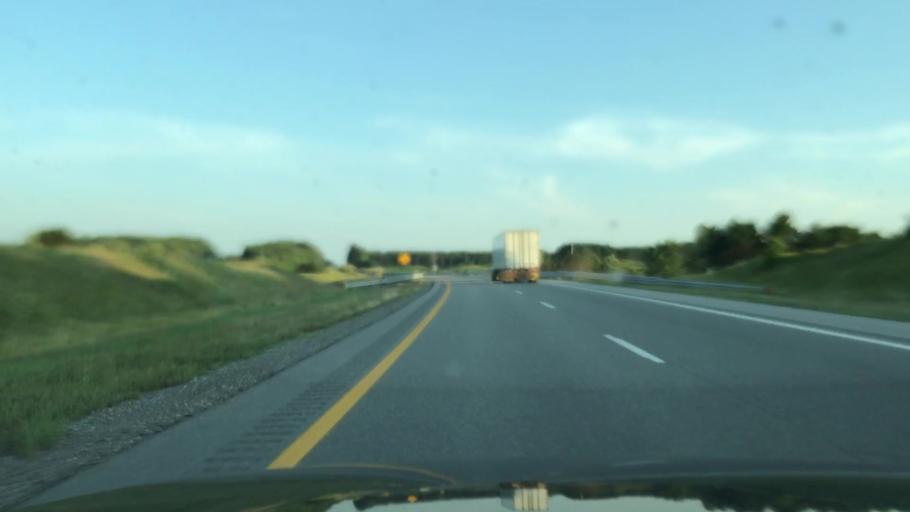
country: US
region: Michigan
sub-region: Osceola County
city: Reed City
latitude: 43.8618
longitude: -85.5357
